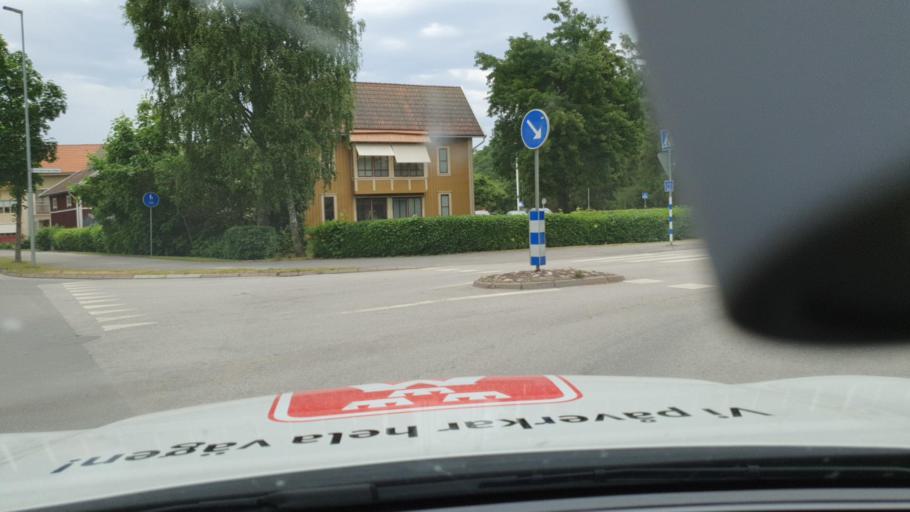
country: SE
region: Vaestra Goetaland
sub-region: Hjo Kommun
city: Hjo
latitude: 58.3070
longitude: 14.2948
